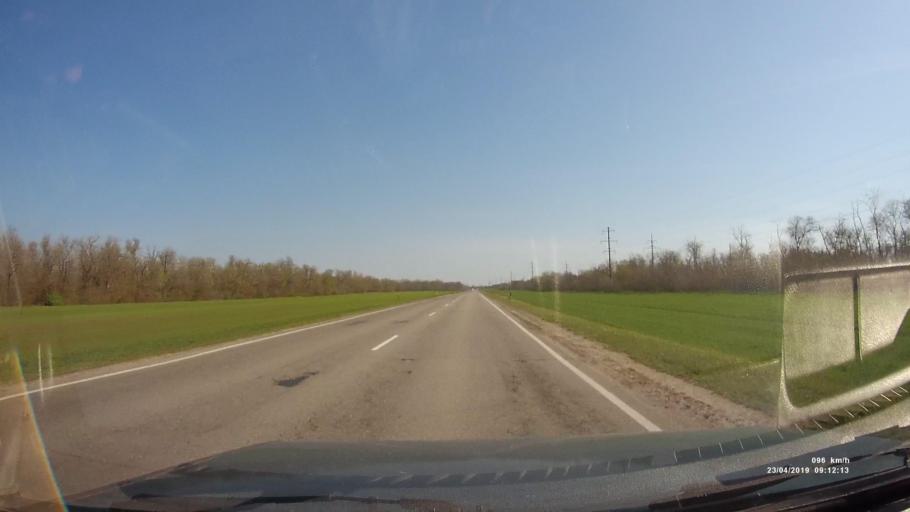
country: RU
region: Rostov
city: Proletarsk
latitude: 46.6047
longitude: 41.6380
